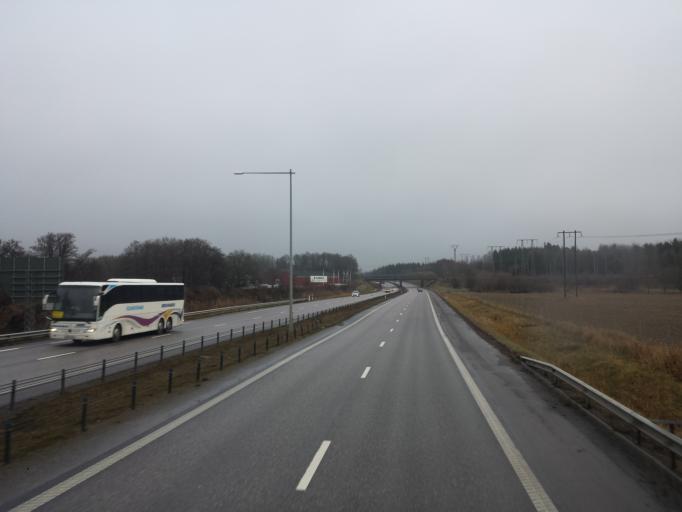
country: SE
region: OEstergoetland
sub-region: Norrkopings Kommun
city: Jursla
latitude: 58.6494
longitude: 16.1766
